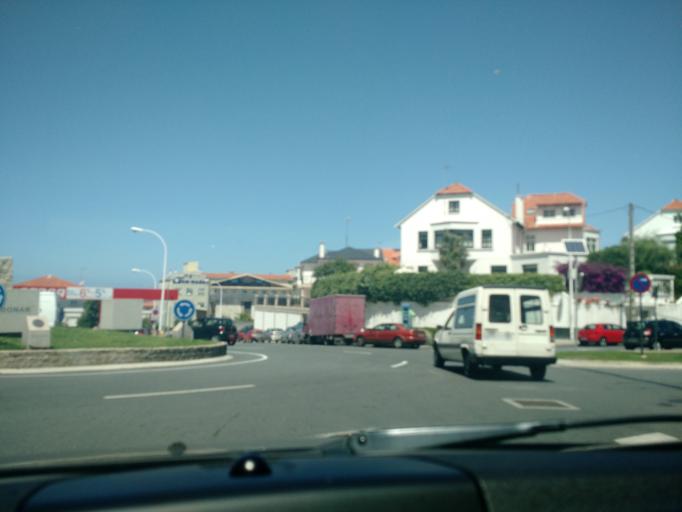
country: ES
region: Galicia
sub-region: Provincia da Coruna
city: A Coruna
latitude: 43.3651
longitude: -8.4187
